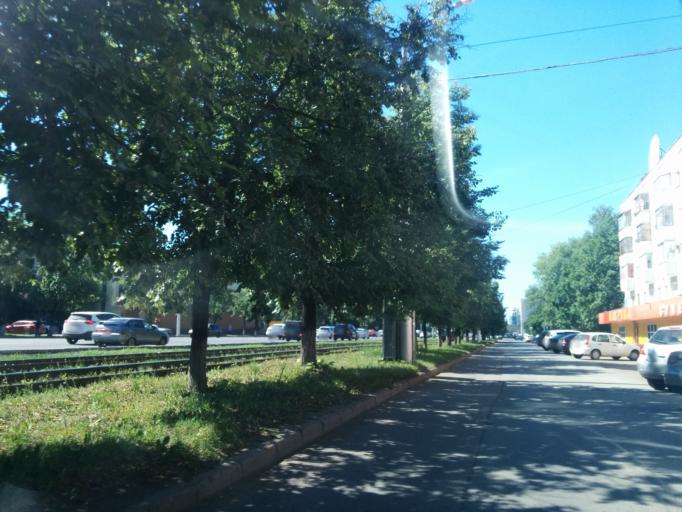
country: RU
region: Bashkortostan
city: Ufa
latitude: 54.7536
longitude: 55.9898
